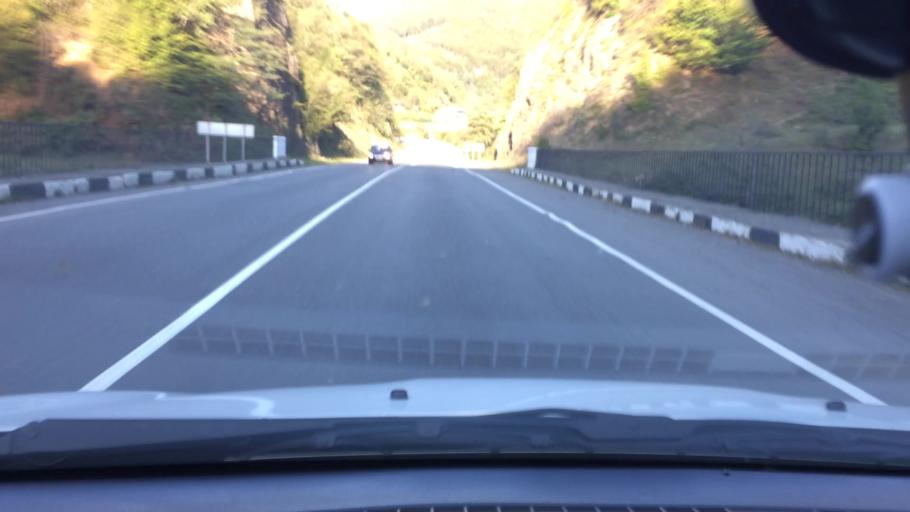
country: GE
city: Surami
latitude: 42.0984
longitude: 43.3967
